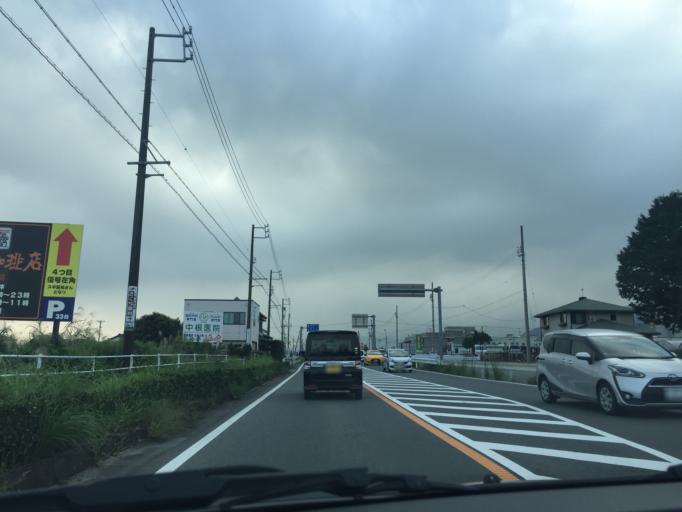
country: JP
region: Aichi
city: Shinshiro
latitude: 34.9119
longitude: 137.5090
